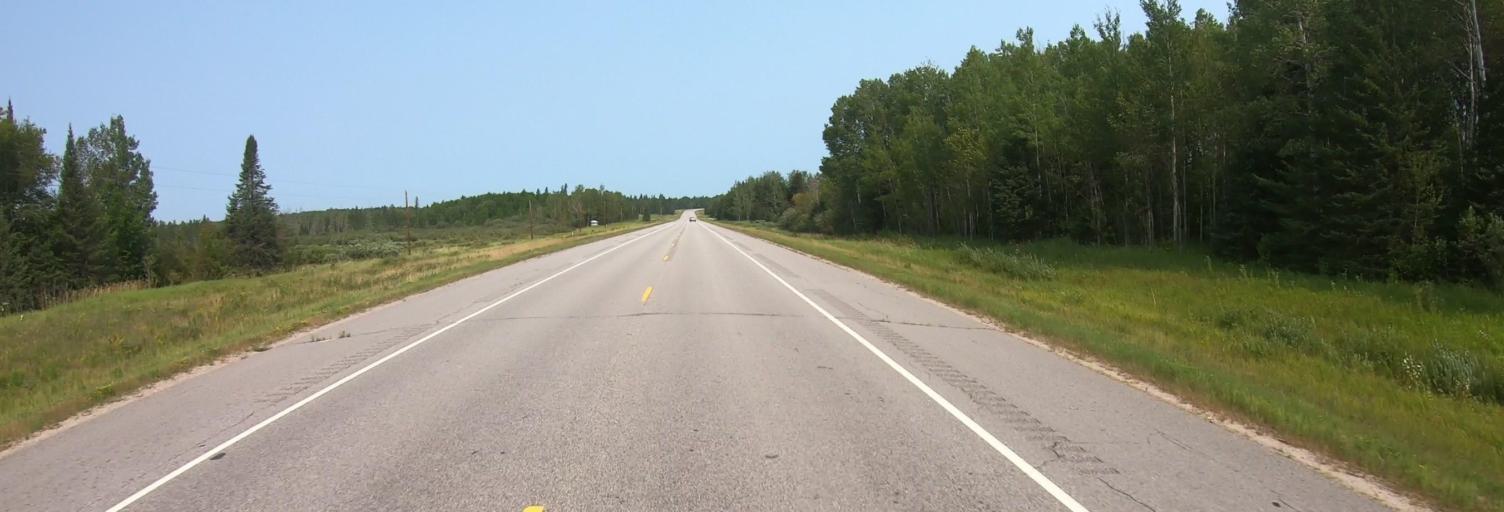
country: CA
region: Ontario
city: Fort Frances
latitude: 48.2875
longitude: -92.9687
